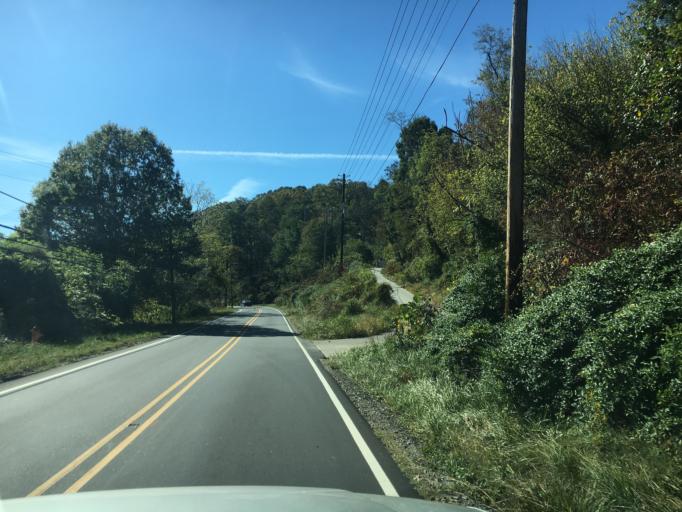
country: US
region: North Carolina
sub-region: Buncombe County
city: Woodfin
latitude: 35.6270
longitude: -82.5853
